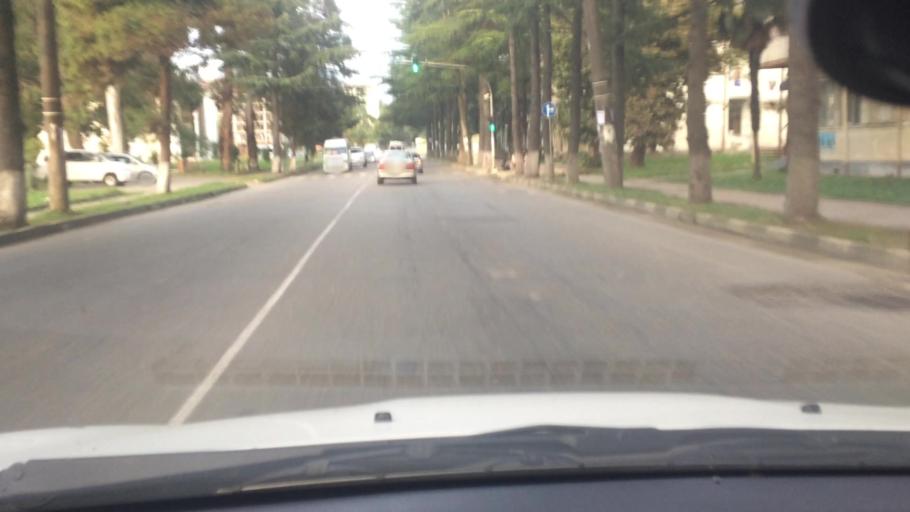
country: GE
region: Ajaria
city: Makhinjauri
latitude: 41.6625
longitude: 41.6806
